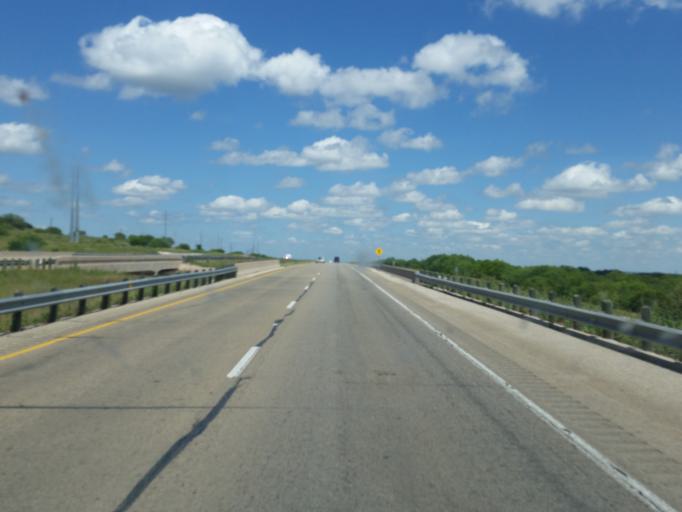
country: US
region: Texas
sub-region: Callahan County
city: Baird
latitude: 32.3915
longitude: -99.3460
